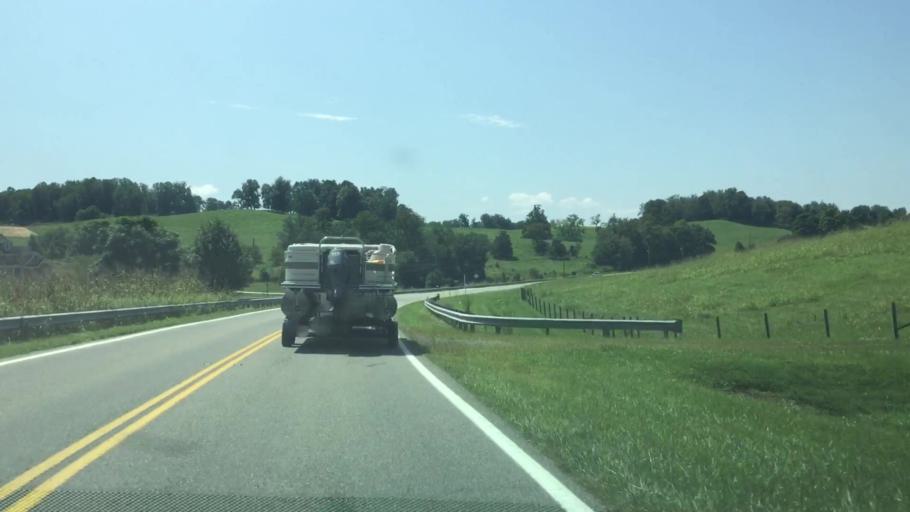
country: US
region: Virginia
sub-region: Washington County
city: Abingdon
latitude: 36.6312
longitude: -81.9975
